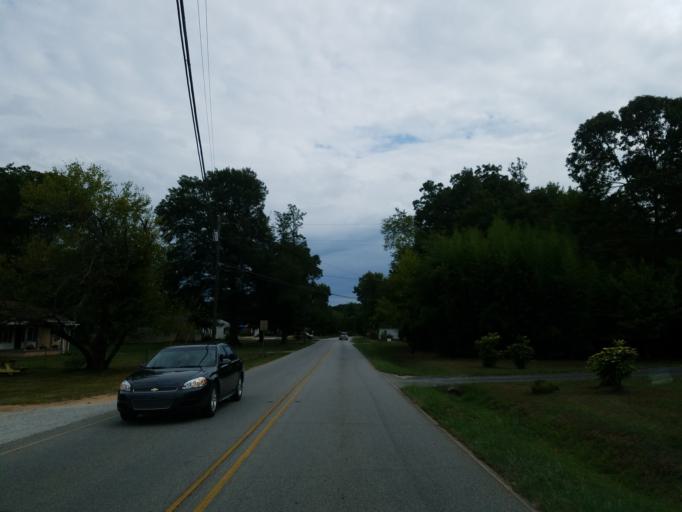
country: US
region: Georgia
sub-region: Henry County
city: Hampton
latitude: 33.3419
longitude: -84.2917
